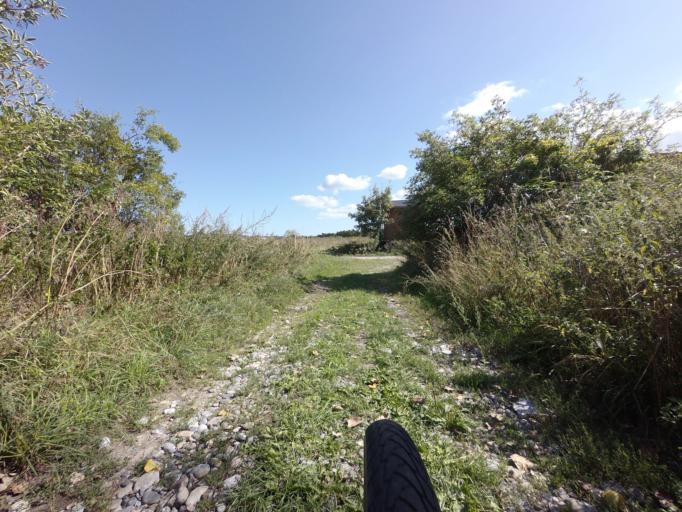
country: DK
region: Zealand
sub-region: Vordingborg Kommune
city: Stege
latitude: 55.0205
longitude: 12.4308
